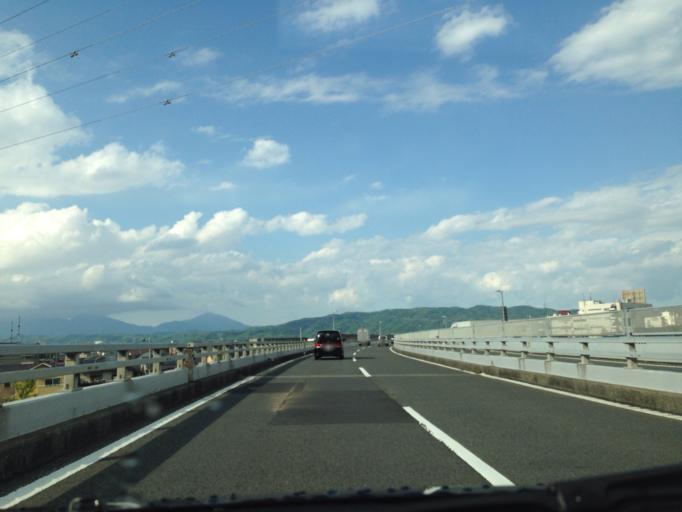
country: JP
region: Kanagawa
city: Odawara
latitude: 35.2804
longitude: 139.1522
